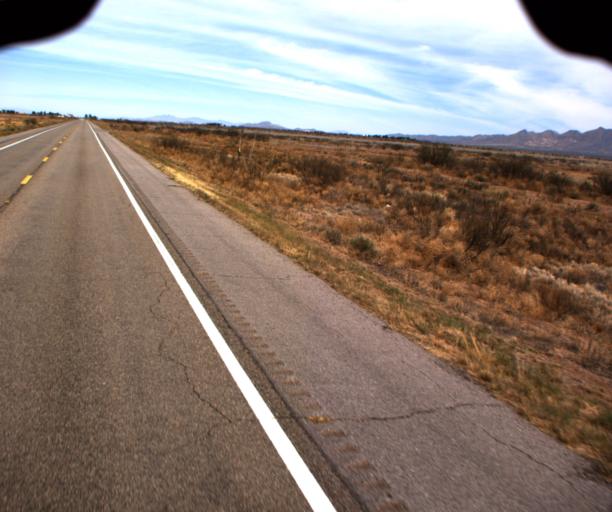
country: US
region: Arizona
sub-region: Cochise County
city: Pirtleville
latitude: 31.5767
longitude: -109.6684
